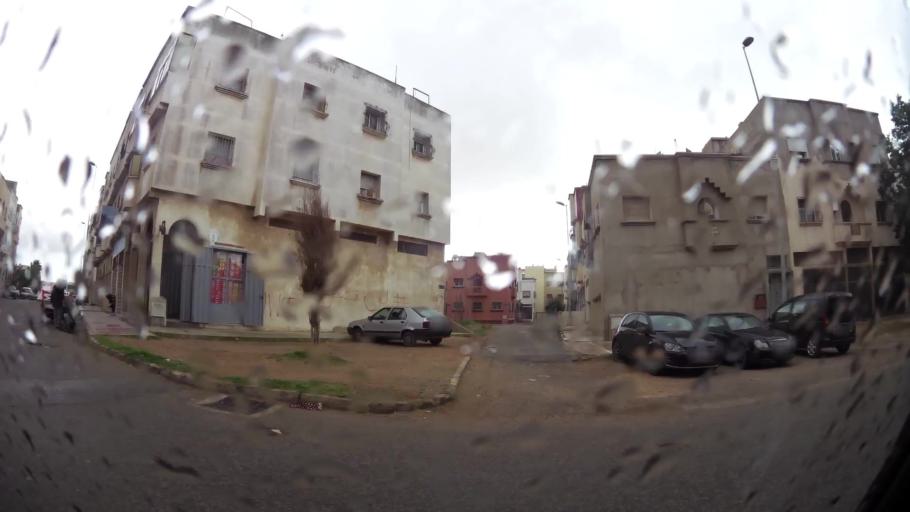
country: MA
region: Grand Casablanca
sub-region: Casablanca
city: Casablanca
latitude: 33.5653
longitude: -7.6907
